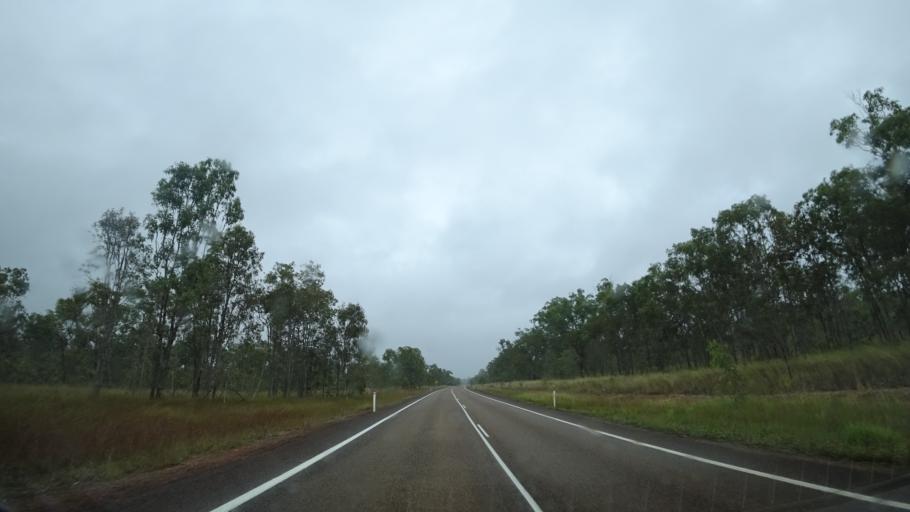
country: AU
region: Queensland
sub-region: Tablelands
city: Ravenshoe
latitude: -17.6929
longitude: 145.2209
